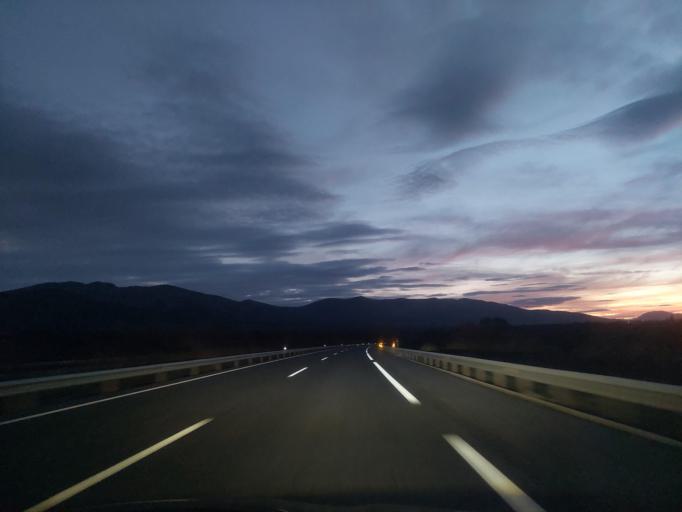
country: ES
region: Castille and Leon
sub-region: Provincia de Segovia
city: Segovia
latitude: 40.8808
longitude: -4.1180
